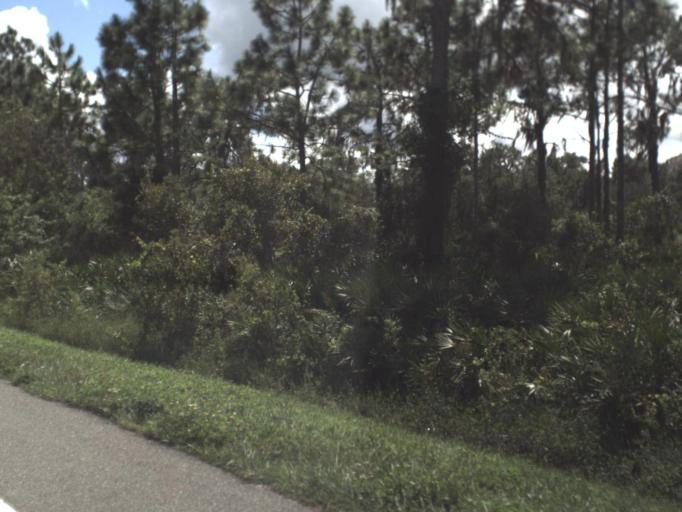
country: US
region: Florida
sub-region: Sarasota County
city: Fruitville
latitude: 27.3943
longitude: -82.2943
